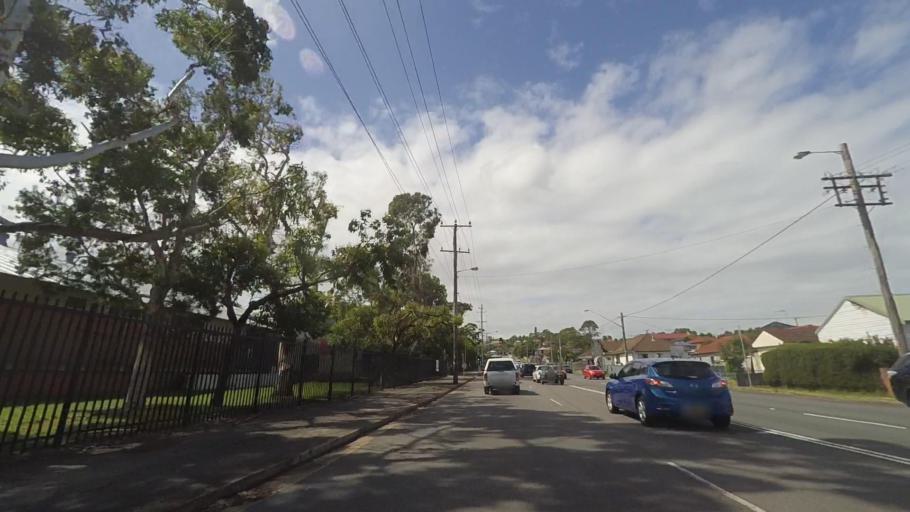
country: AU
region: New South Wales
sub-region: Newcastle
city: North Lambton
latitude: -32.9122
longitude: 151.7047
